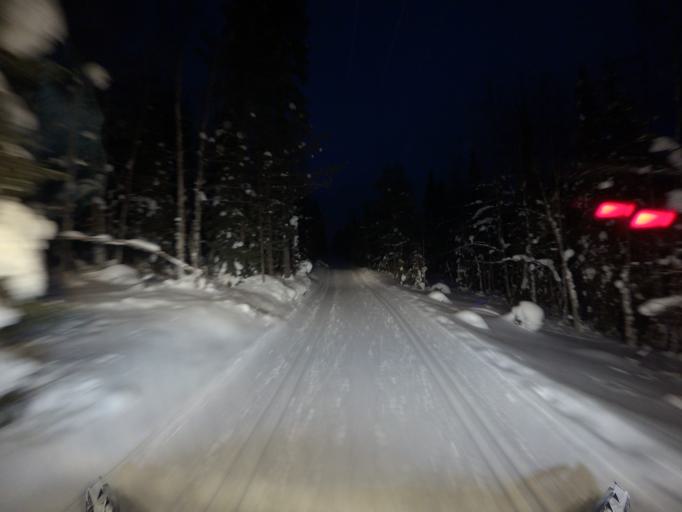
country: FI
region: Lapland
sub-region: Tunturi-Lappi
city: Kolari
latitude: 67.5863
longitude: 24.0876
